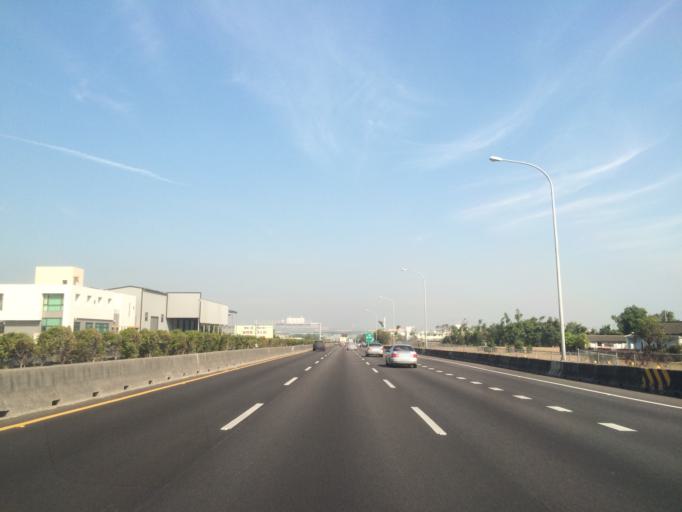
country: TW
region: Taiwan
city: Fengyuan
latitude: 24.2554
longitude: 120.6911
